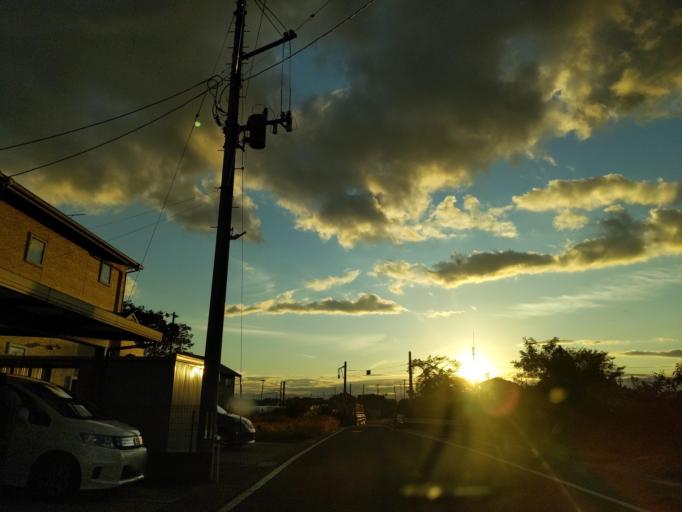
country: JP
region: Fukushima
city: Motomiya
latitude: 37.4967
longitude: 140.3979
